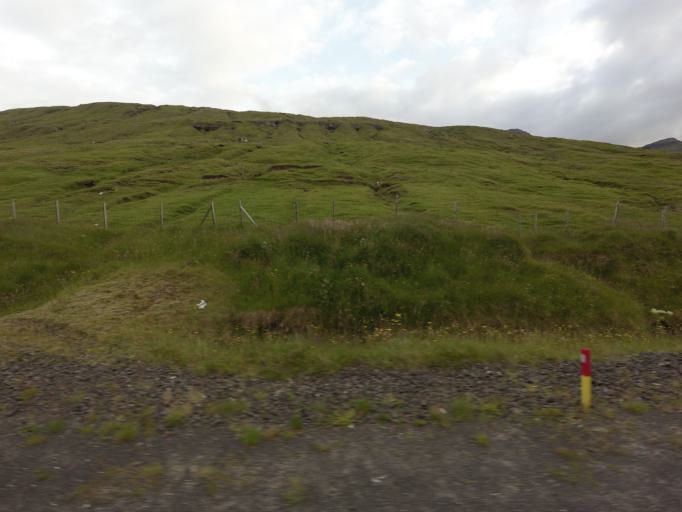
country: FO
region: Streymoy
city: Kollafjordhur
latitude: 62.1710
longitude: -6.9693
